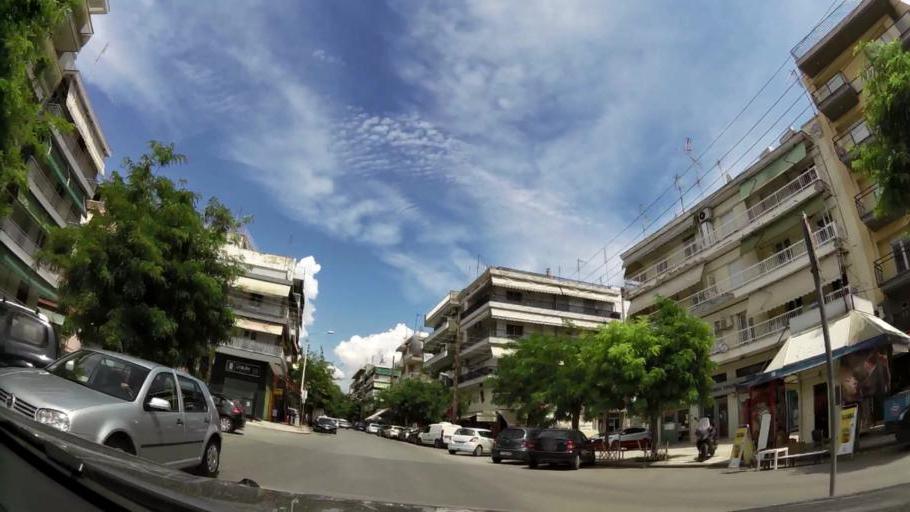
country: GR
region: Central Macedonia
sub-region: Nomos Thessalonikis
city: Triandria
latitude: 40.6093
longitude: 22.9699
